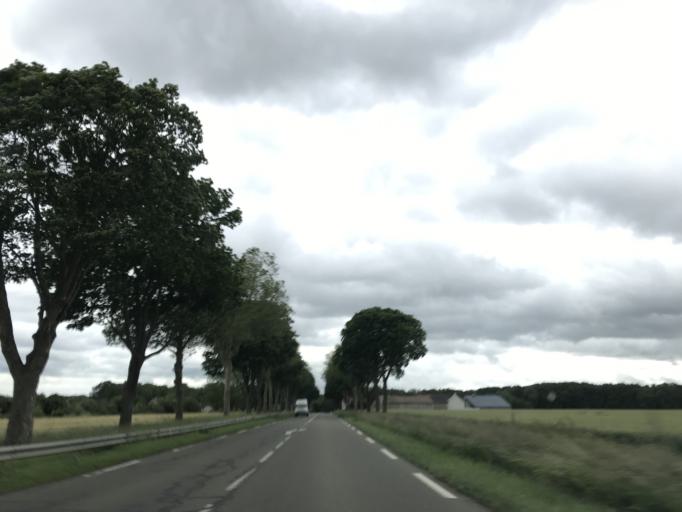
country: FR
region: Ile-de-France
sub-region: Departement des Yvelines
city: Bennecourt
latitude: 49.0262
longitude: 1.5318
